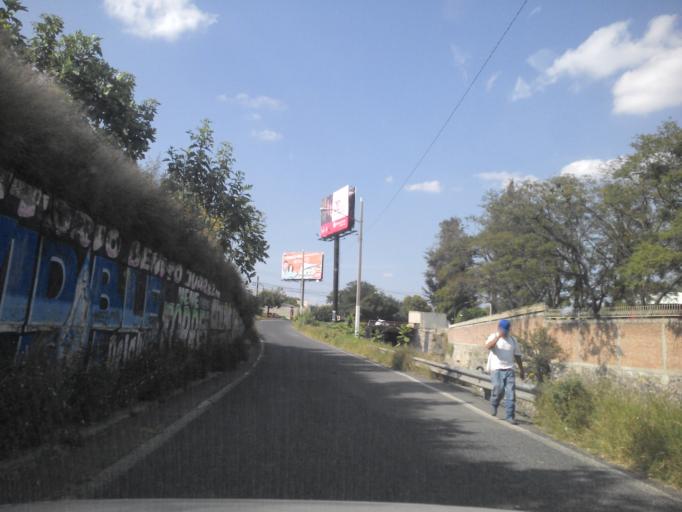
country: MX
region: Jalisco
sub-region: Tlajomulco de Zuniga
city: La Tijera
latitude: 20.6149
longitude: -103.4255
